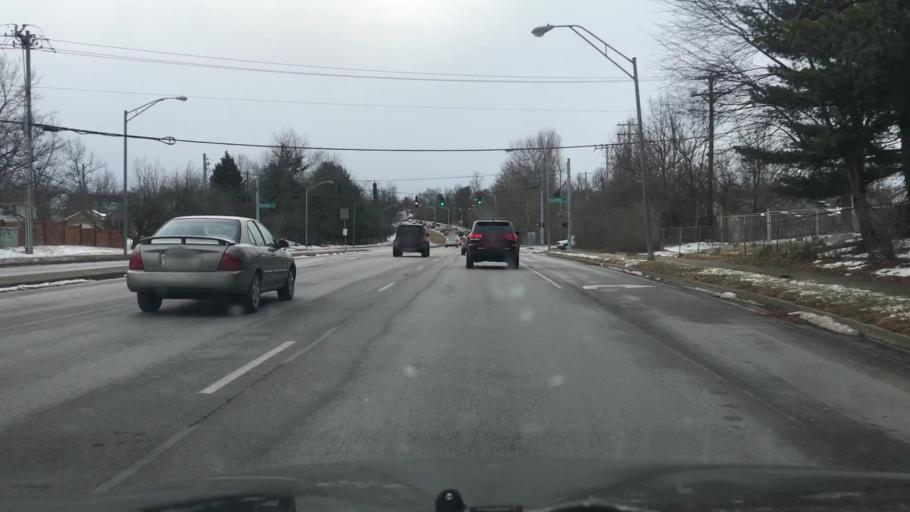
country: US
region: Kentucky
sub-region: Fayette County
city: Lexington
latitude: 37.9945
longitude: -84.4521
